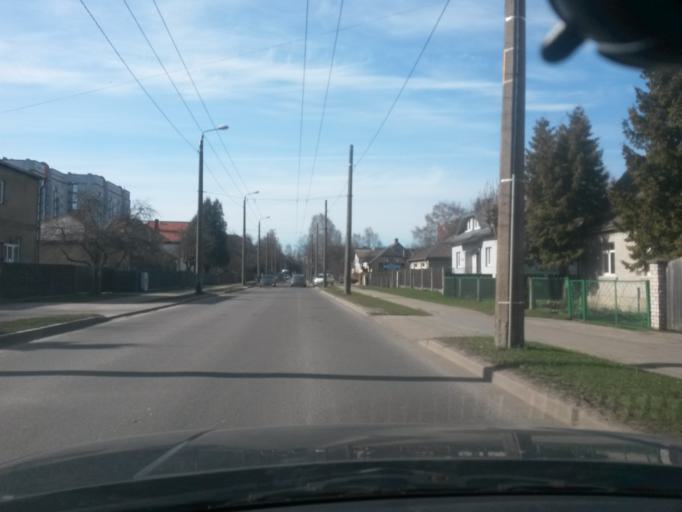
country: LV
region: Kekava
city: Balozi
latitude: 56.9074
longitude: 24.1988
